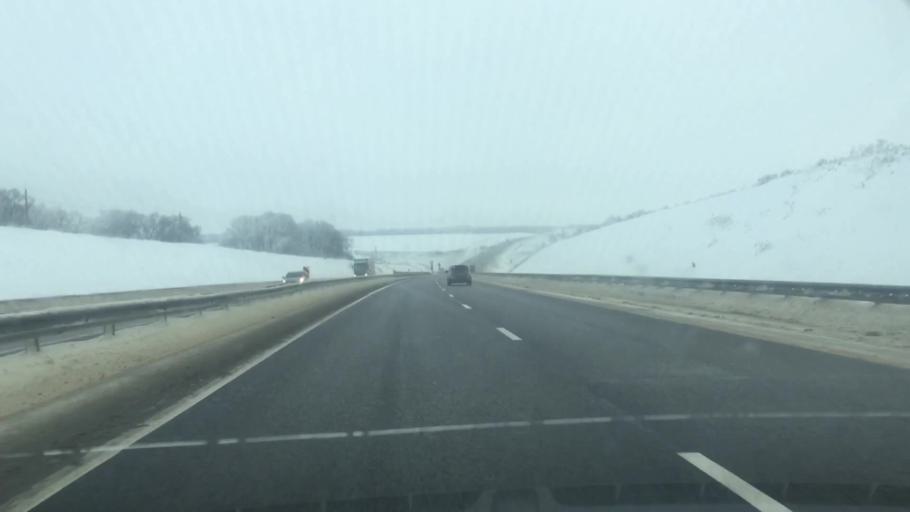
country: RU
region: Lipetsk
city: Stanovoye
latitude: 52.8724
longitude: 38.2789
